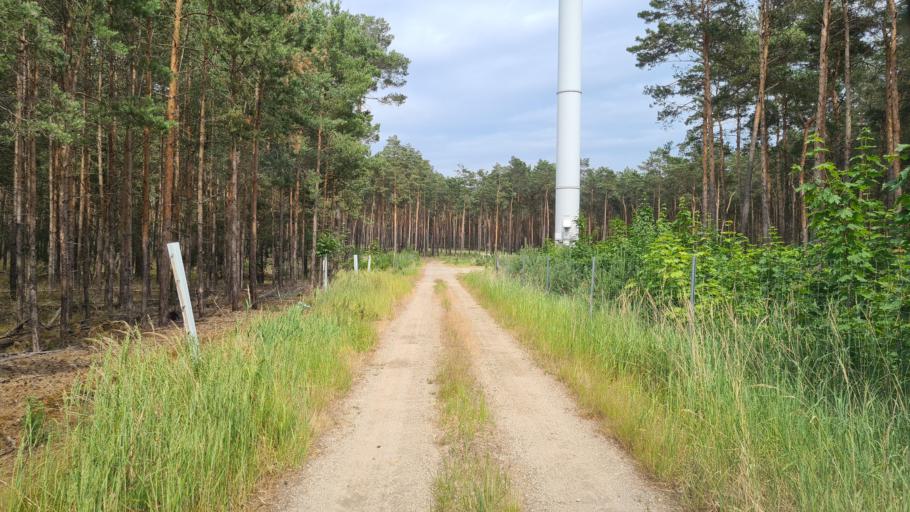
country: DE
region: Brandenburg
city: Schilda
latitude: 51.6601
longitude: 13.3482
